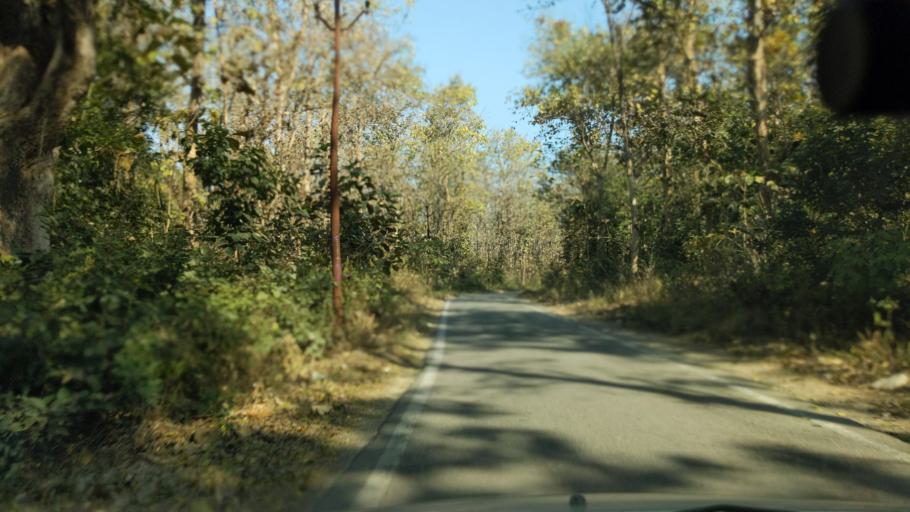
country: IN
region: Uttarakhand
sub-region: Naini Tal
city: Ramnagar
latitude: 29.4044
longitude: 79.1371
